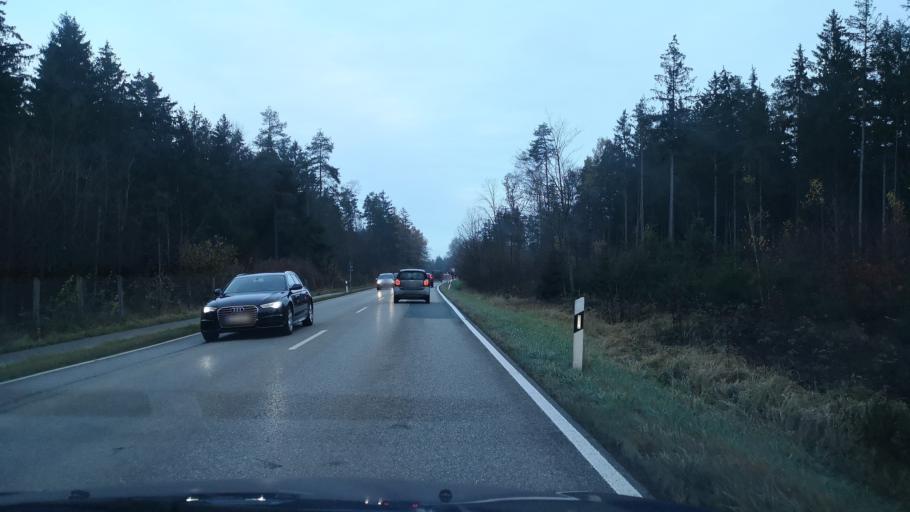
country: DE
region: Bavaria
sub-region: Upper Bavaria
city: Forstinning
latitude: 48.1495
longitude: 11.9160
